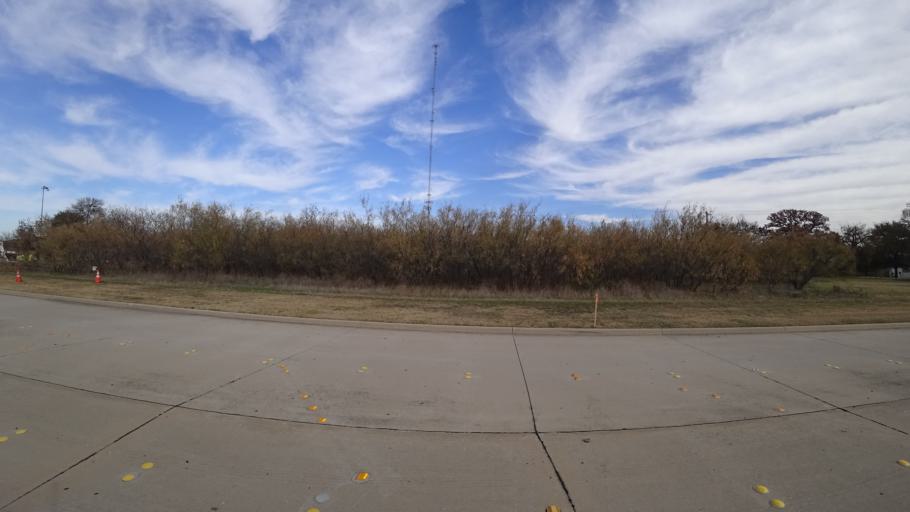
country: US
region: Texas
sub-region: Denton County
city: Lewisville
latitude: 33.0380
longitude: -96.9730
